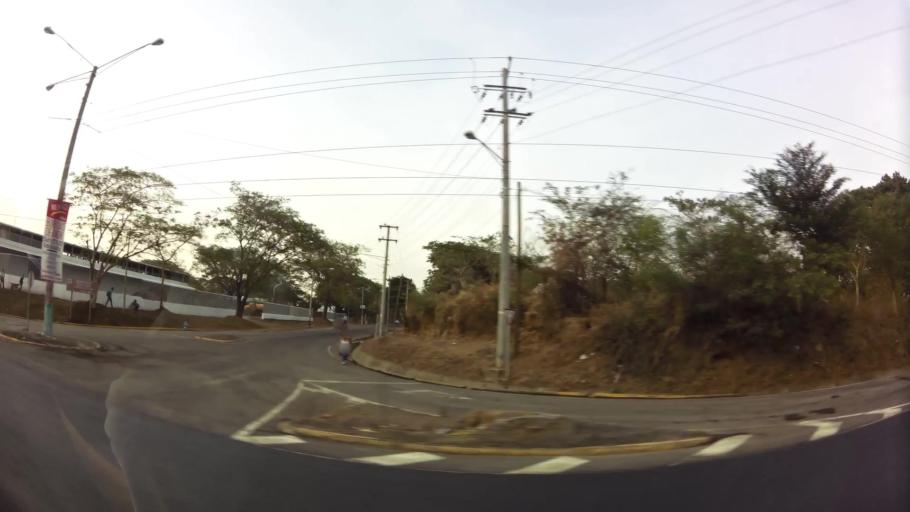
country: NI
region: Managua
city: Ciudad Sandino
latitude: 12.1735
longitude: -86.3468
